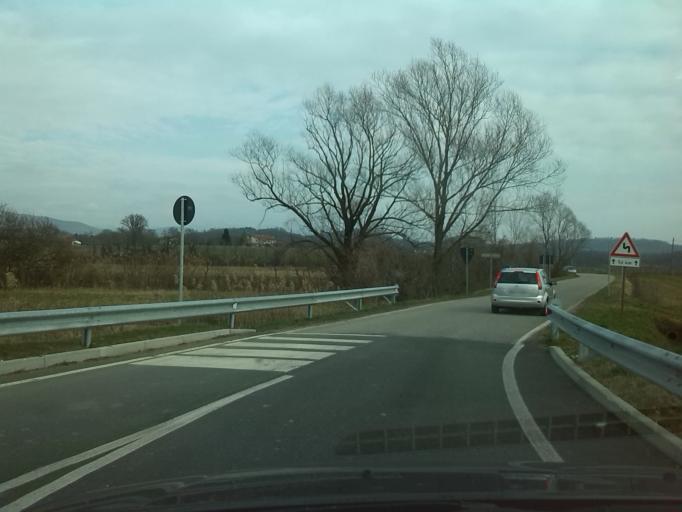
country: IT
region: Friuli Venezia Giulia
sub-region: Provincia di Gorizia
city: Mossa
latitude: 45.9630
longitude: 13.5432
